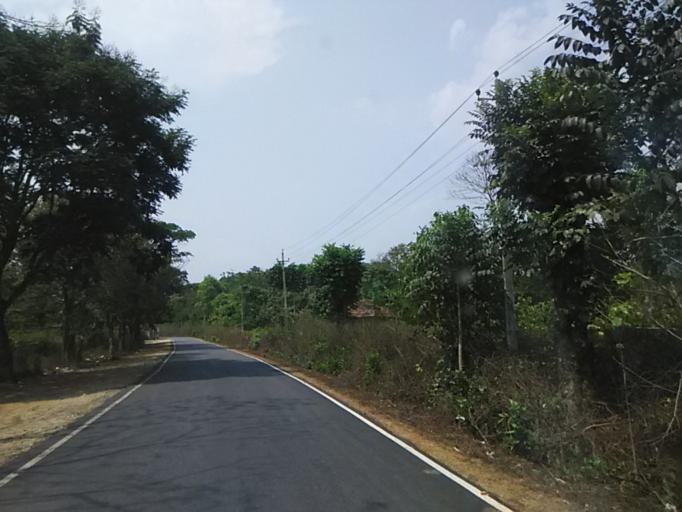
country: IN
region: Karnataka
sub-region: Kodagu
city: Virarajendrapet
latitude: 12.1476
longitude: 75.7950
